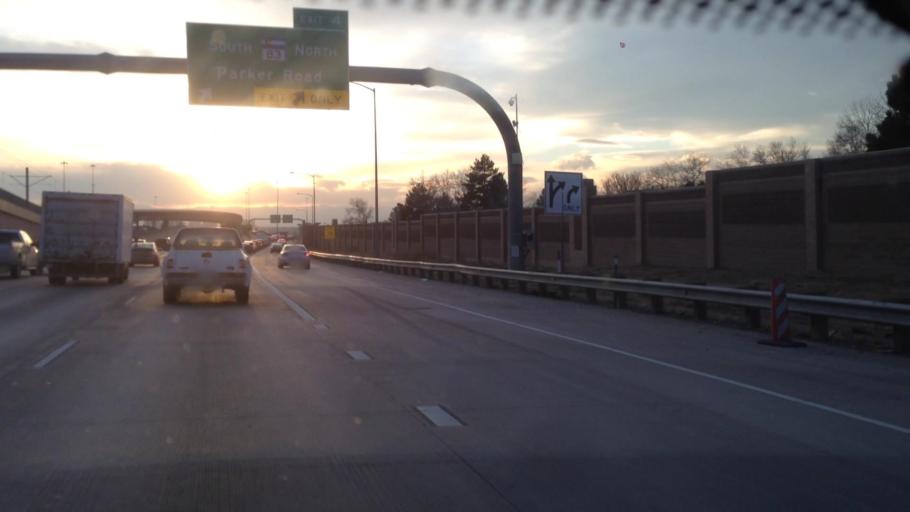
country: US
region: Colorado
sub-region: Adams County
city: Aurora
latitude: 39.6613
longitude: -104.8382
